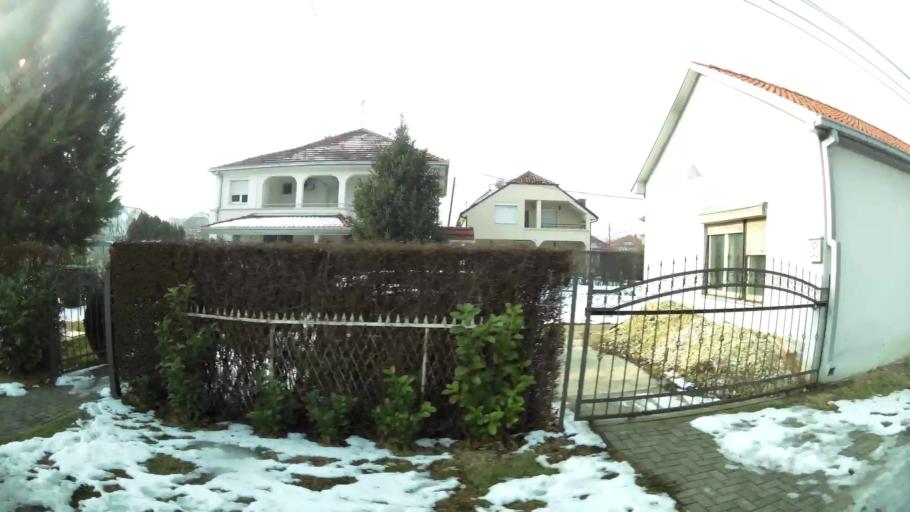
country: MK
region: Ilinden
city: Ilinden
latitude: 41.9917
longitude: 21.5851
